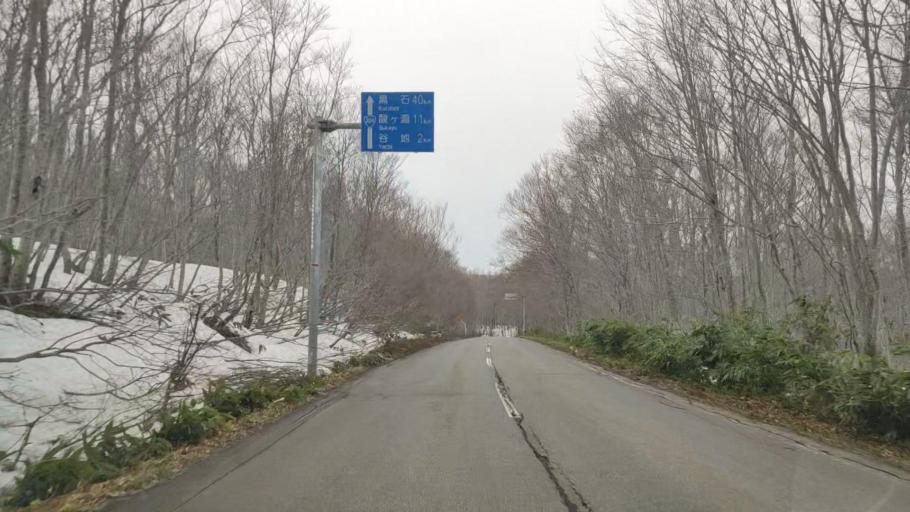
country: JP
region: Aomori
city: Aomori Shi
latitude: 40.6462
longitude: 140.9440
